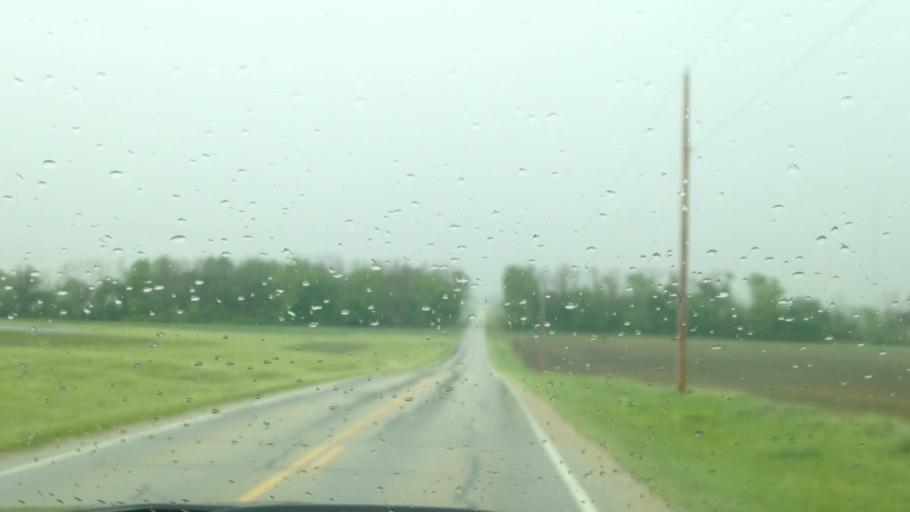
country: US
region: Ohio
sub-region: Darke County
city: Greenville
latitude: 40.1505
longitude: -84.6228
